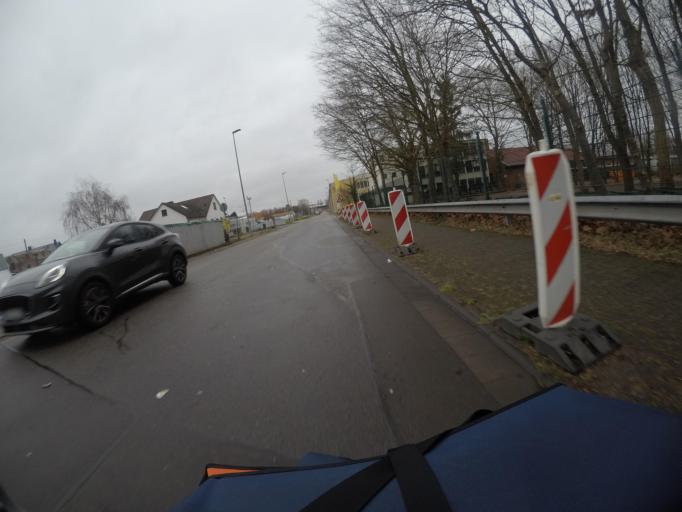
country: DE
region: Rheinland-Pfalz
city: Germersheim
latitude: 49.2247
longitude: 8.3765
